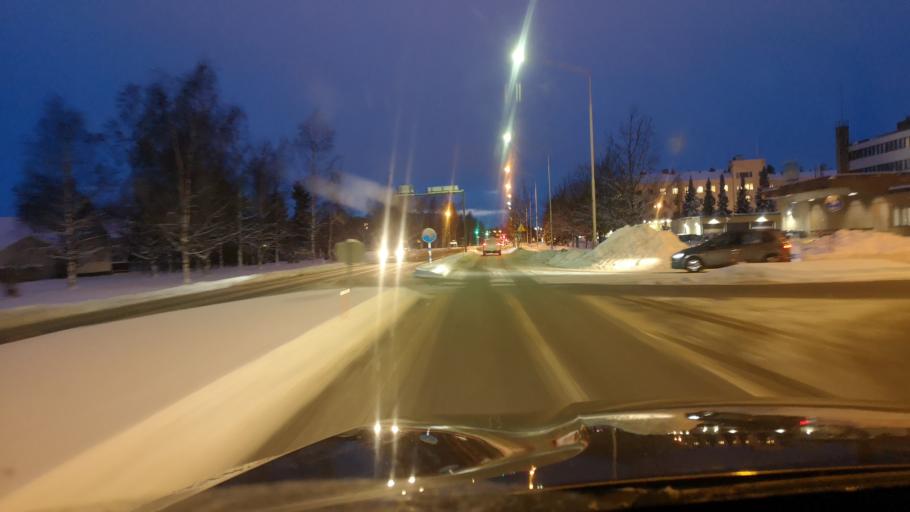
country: FI
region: Varsinais-Suomi
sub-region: Loimaa
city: Loimaa
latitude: 60.8501
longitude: 23.0527
